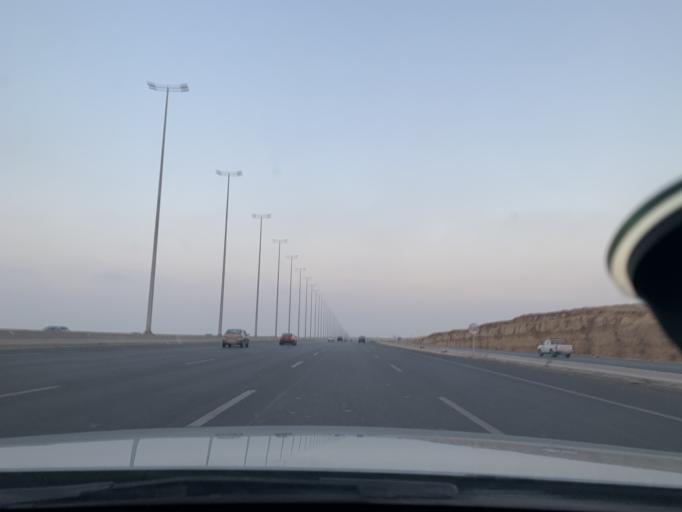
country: EG
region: Muhafazat al Qalyubiyah
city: Al Khankah
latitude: 30.0939
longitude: 31.4911
